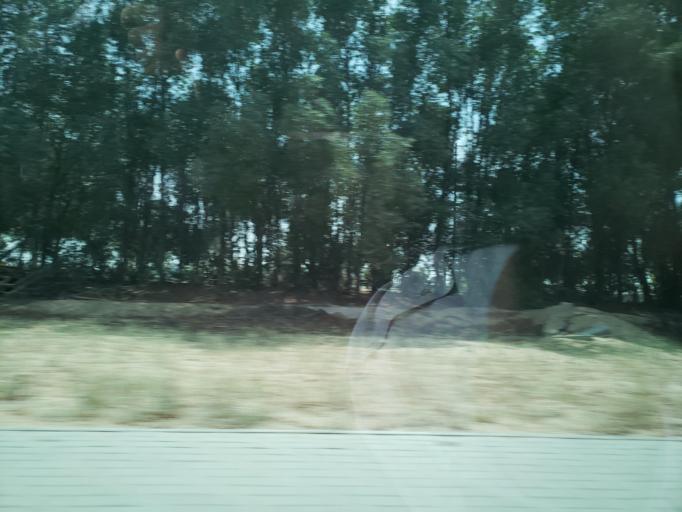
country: AE
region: Ash Shariqah
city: Sharjah
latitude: 25.3242
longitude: 55.4952
